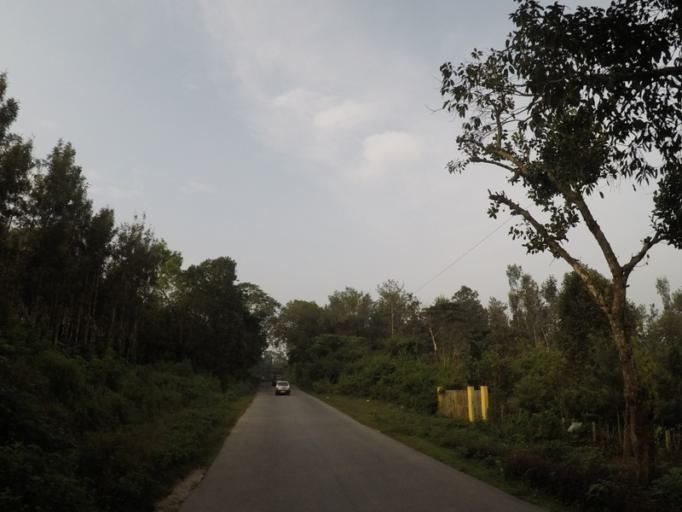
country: IN
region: Karnataka
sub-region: Chikmagalur
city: Chikmagalur
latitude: 13.2683
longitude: 75.6913
